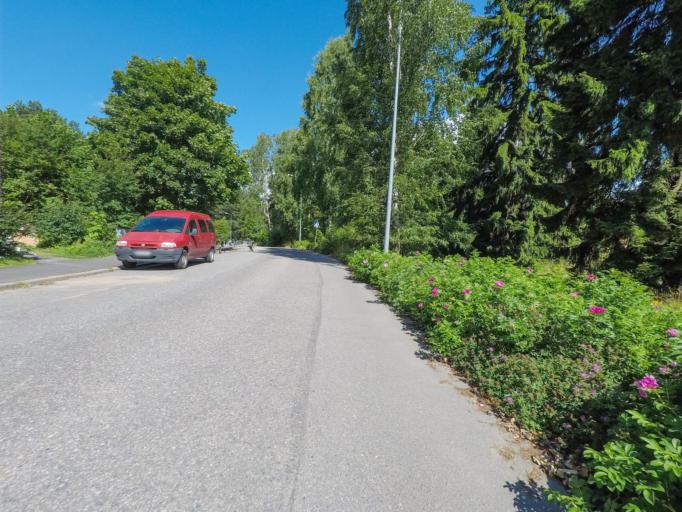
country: FI
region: Uusimaa
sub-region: Helsinki
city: Vantaa
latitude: 60.1925
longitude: 25.0705
